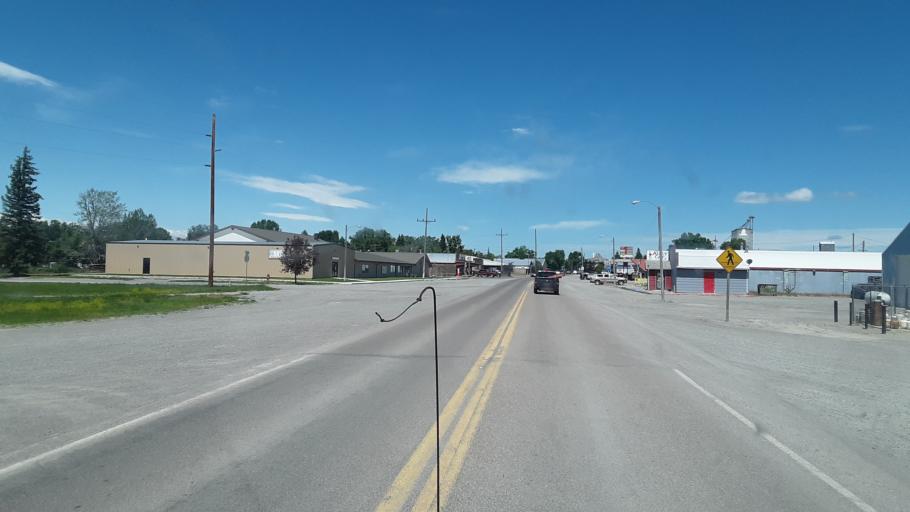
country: US
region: Montana
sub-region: Teton County
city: Choteau
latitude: 47.8059
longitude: -112.1778
